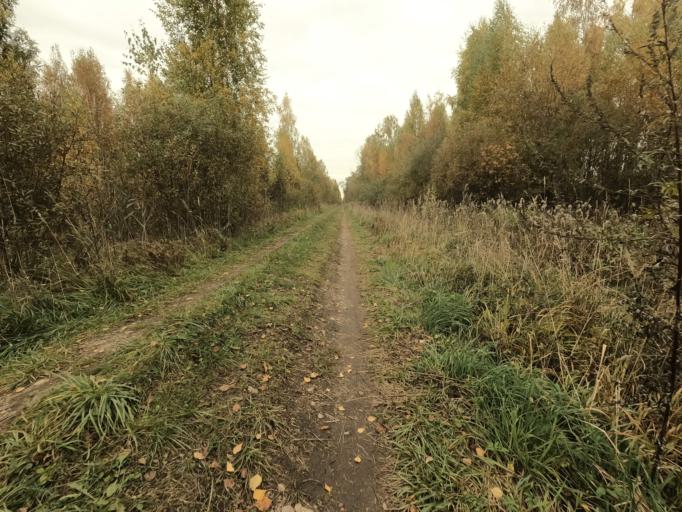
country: RU
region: Novgorod
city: Pankovka
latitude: 58.8849
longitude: 30.9459
